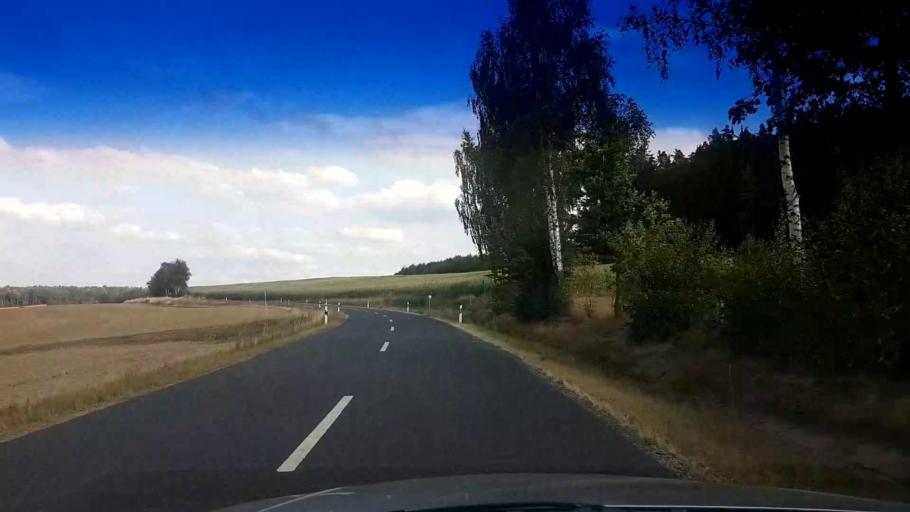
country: DE
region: Bavaria
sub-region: Upper Palatinate
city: Waldsassen
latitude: 50.0220
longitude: 12.3481
